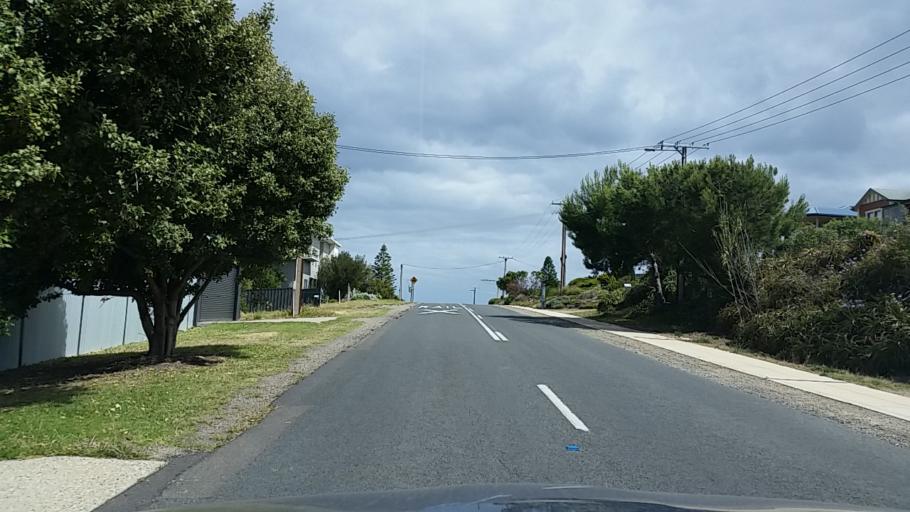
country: AU
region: South Australia
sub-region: Alexandrina
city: Port Elliot
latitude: -35.5336
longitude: 138.6774
